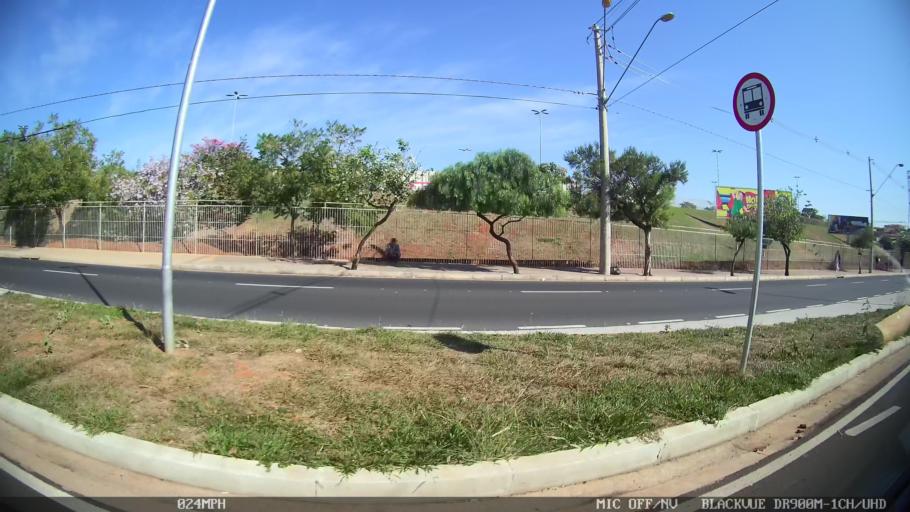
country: BR
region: Sao Paulo
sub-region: Sao Jose Do Rio Preto
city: Sao Jose do Rio Preto
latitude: -20.7686
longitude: -49.3850
